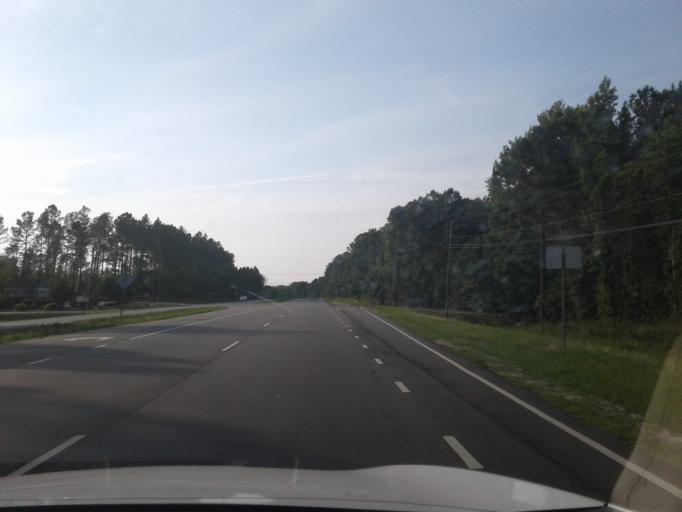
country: US
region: North Carolina
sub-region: Harnett County
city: Erwin
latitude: 35.3394
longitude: -78.6776
